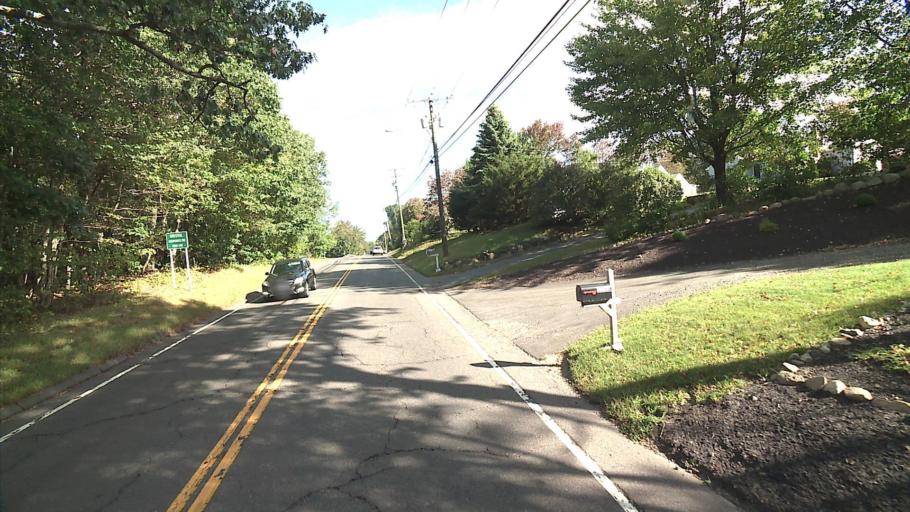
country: US
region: Connecticut
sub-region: Hartford County
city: Bristol
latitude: 41.6412
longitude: -72.9639
